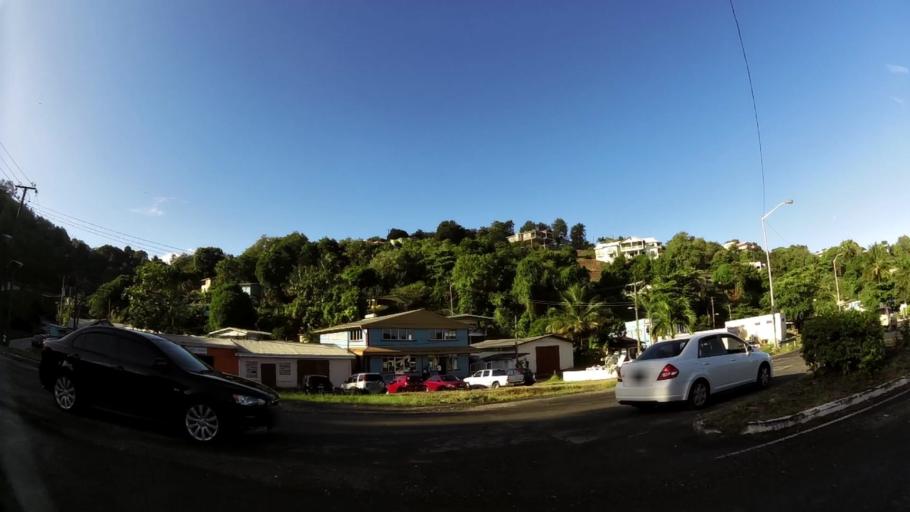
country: LC
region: Castries Quarter
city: Castries
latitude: 14.0104
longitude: -60.9998
